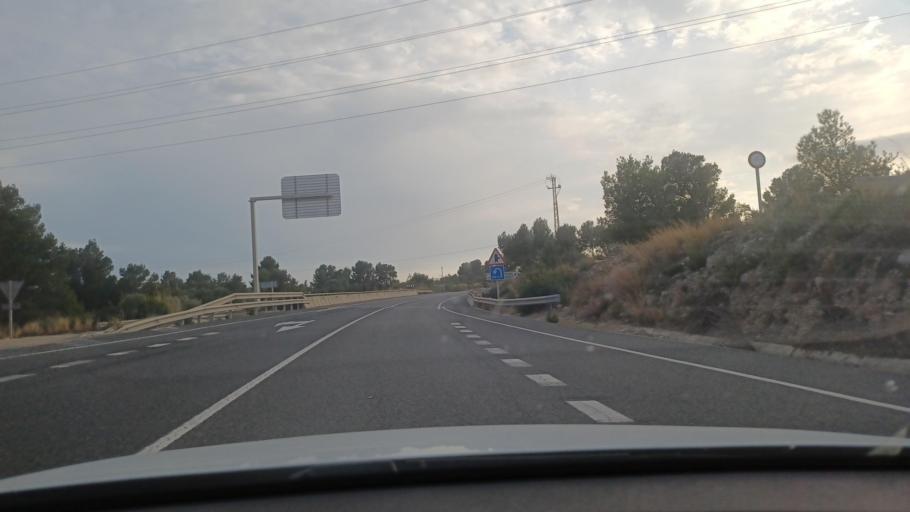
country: ES
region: Catalonia
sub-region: Provincia de Tarragona
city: l'Ametlla de Mar
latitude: 40.9570
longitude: 0.8703
